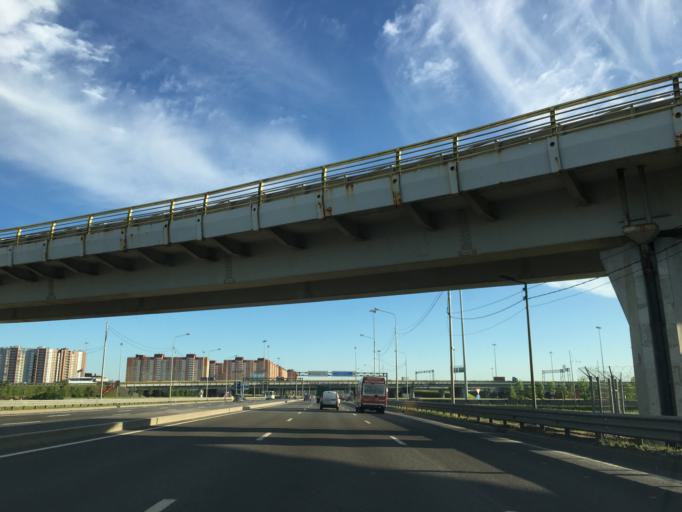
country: RU
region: St.-Petersburg
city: Sosnovaya Polyana
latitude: 59.8024
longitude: 30.1595
